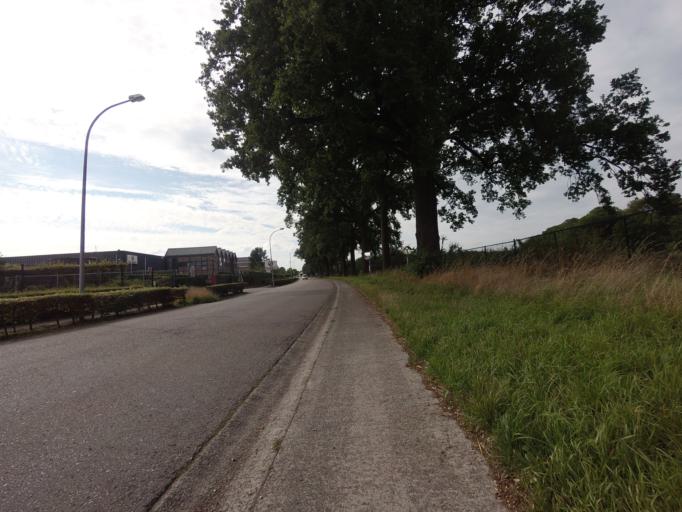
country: BE
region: Flanders
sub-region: Provincie Vlaams-Brabant
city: Londerzeel
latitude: 51.0160
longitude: 4.3260
